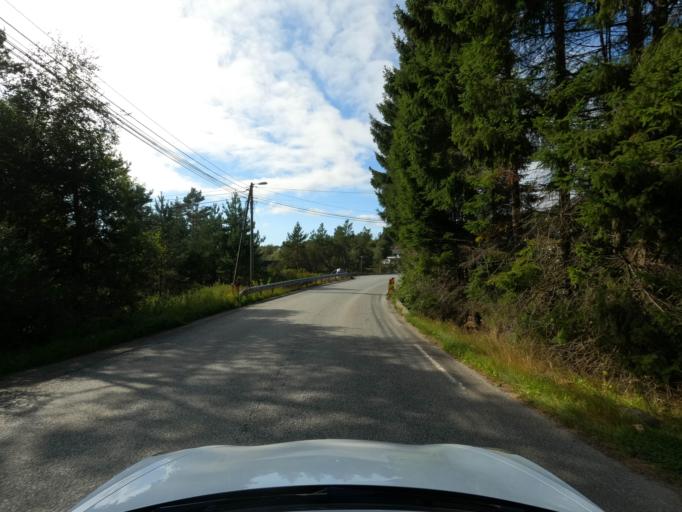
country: NO
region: Hordaland
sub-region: Bergen
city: Ytrebygda
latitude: 60.2676
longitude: 5.2525
